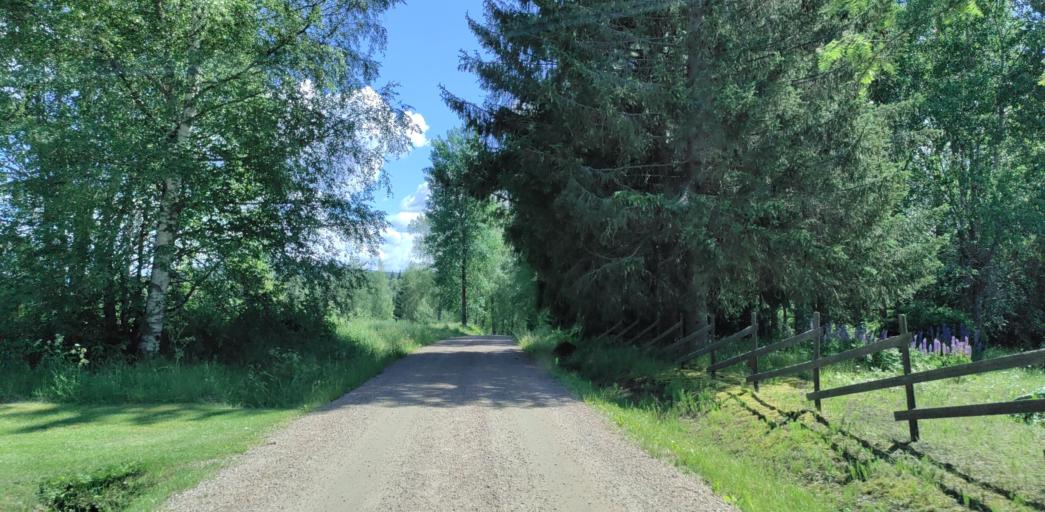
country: SE
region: Vaermland
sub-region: Munkfors Kommun
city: Munkfors
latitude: 59.9508
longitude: 13.4948
